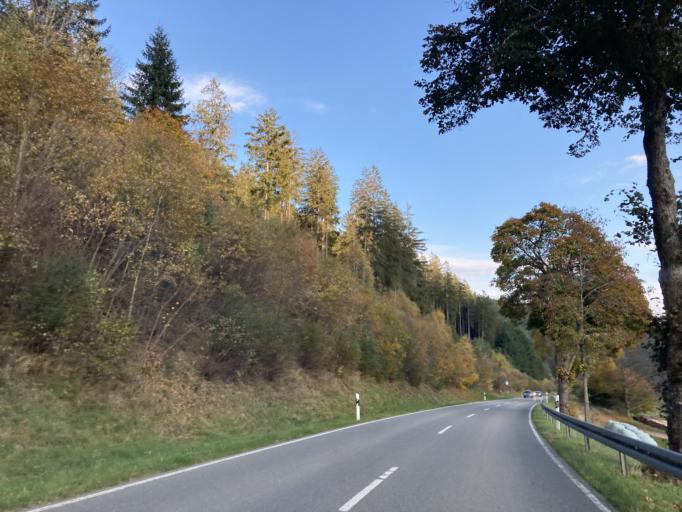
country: DE
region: Baden-Wuerttemberg
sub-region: Freiburg Region
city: Vohrenbach
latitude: 48.0073
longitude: 8.2913
